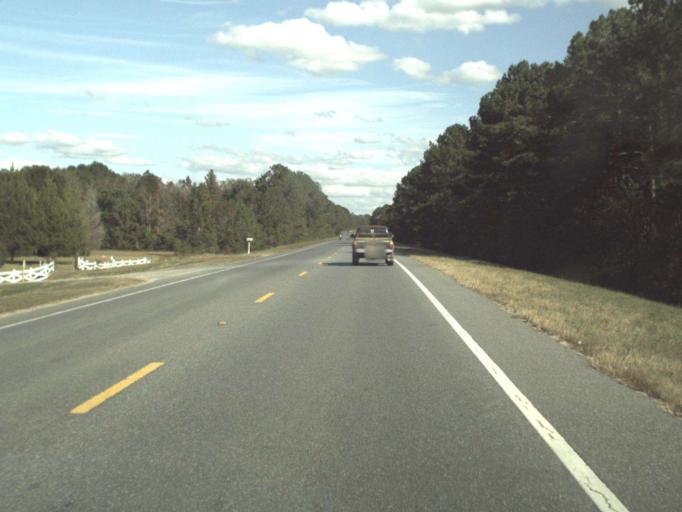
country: US
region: Florida
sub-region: Washington County
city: Chipley
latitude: 30.7776
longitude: -85.6021
